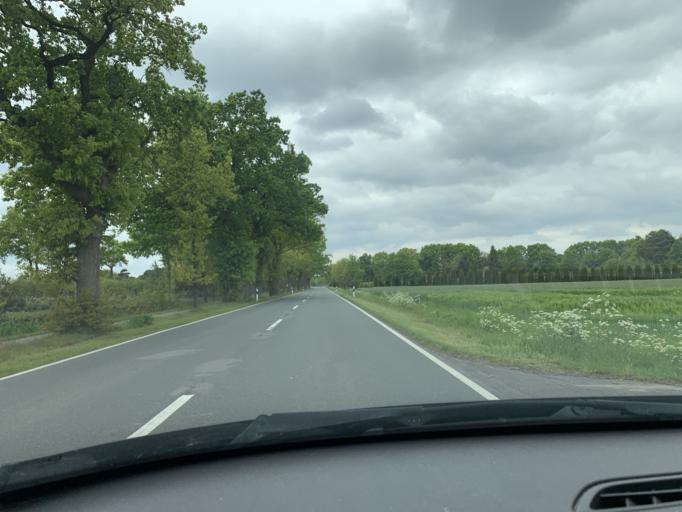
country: DE
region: Lower Saxony
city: Bad Zwischenahn
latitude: 53.1858
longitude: 8.0620
